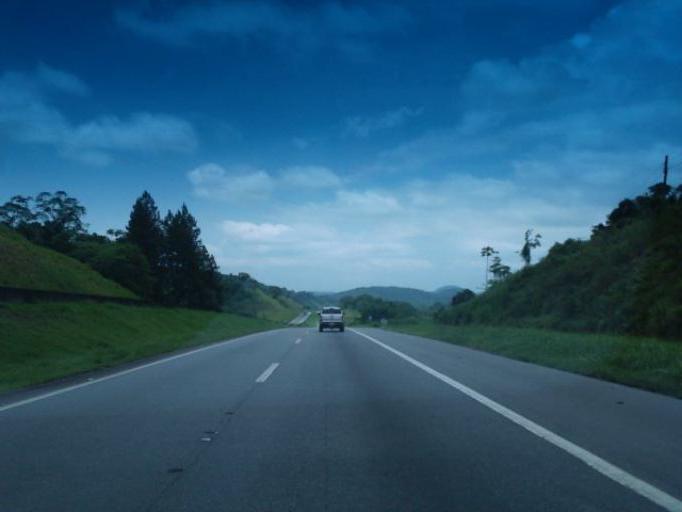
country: BR
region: Sao Paulo
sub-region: Miracatu
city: Miracatu
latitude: -24.1691
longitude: -47.3377
